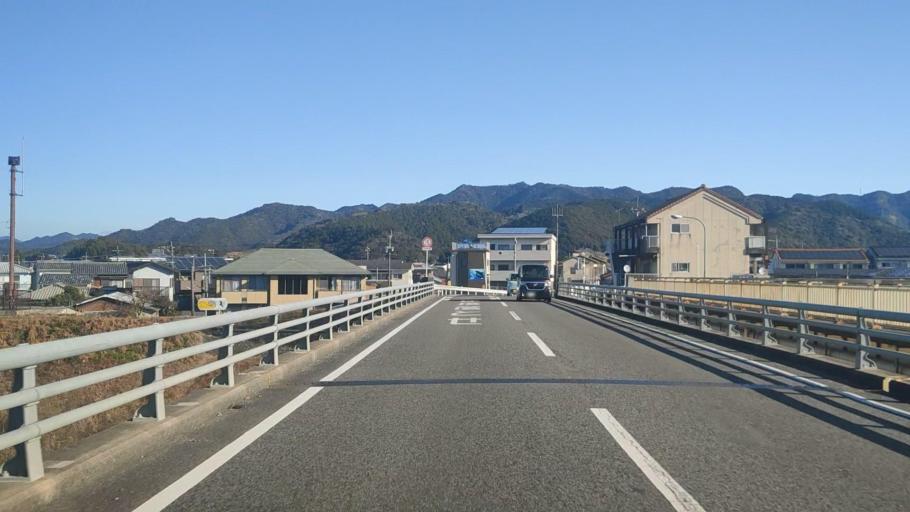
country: JP
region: Miyazaki
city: Nobeoka
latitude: 32.6137
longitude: 131.6902
